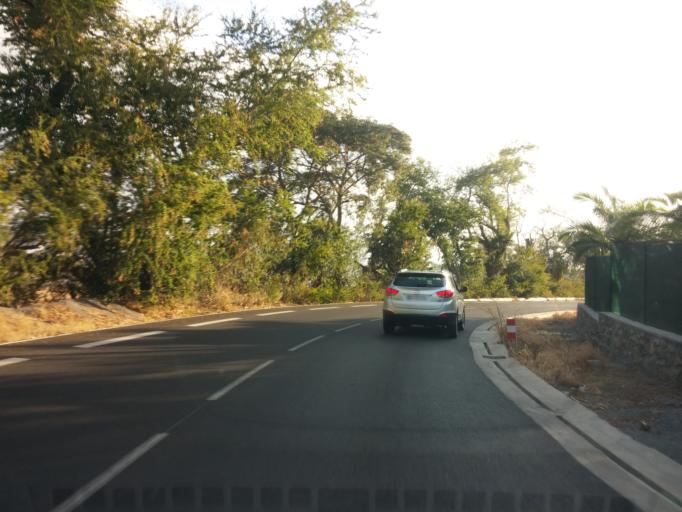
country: RE
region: Reunion
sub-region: Reunion
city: Le Port
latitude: -20.9737
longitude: 55.3056
